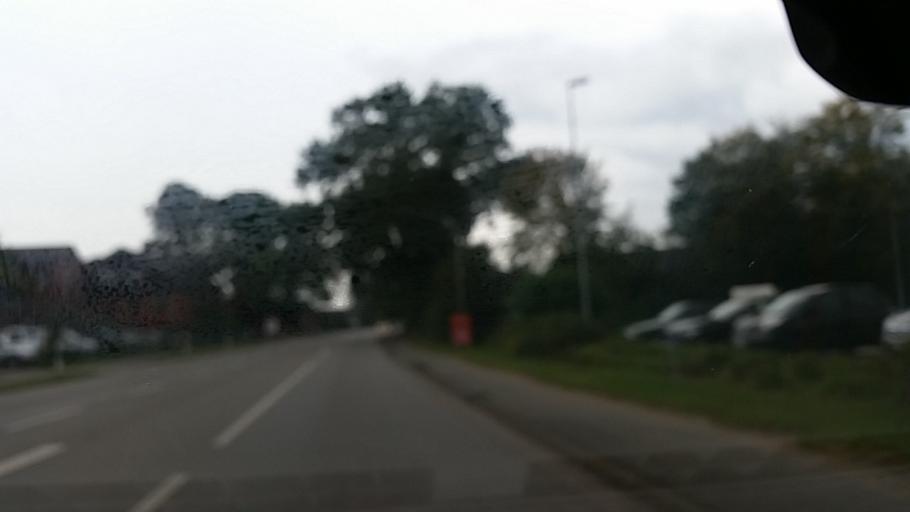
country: DE
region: Schleswig-Holstein
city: Itzstedt
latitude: 53.8111
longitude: 10.1641
